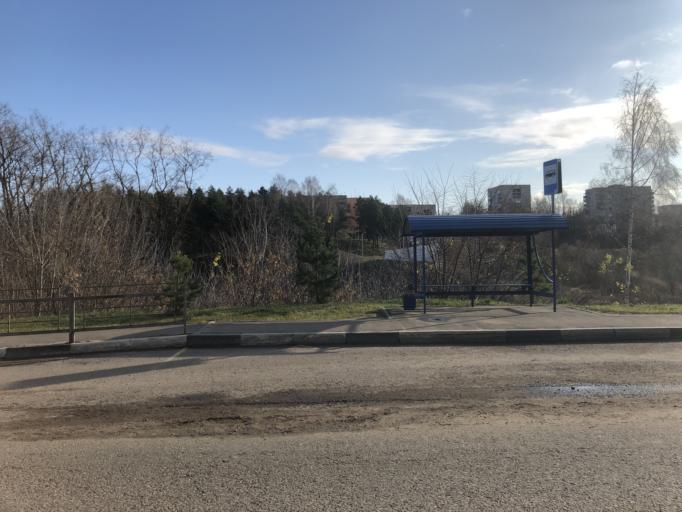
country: RU
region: Tverskaya
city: Rzhev
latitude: 56.2616
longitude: 34.3397
